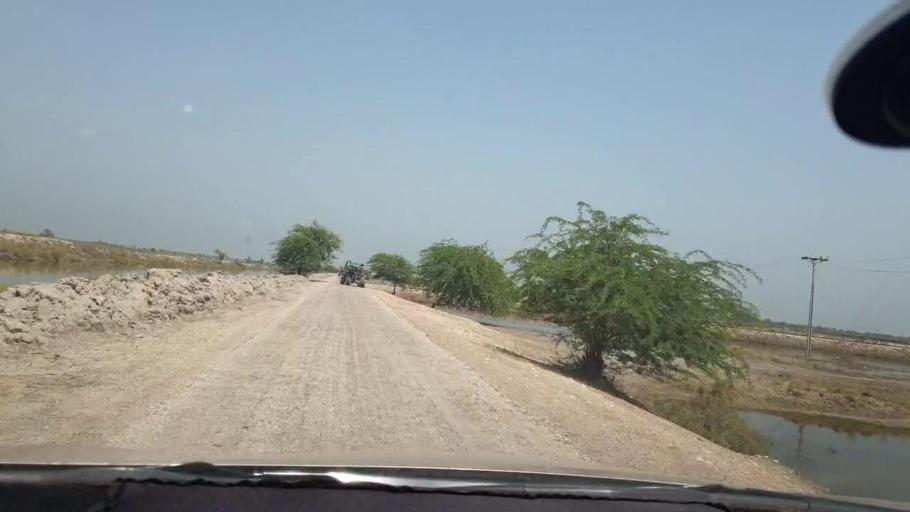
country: PK
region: Sindh
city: Kambar
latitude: 27.6822
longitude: 67.9210
